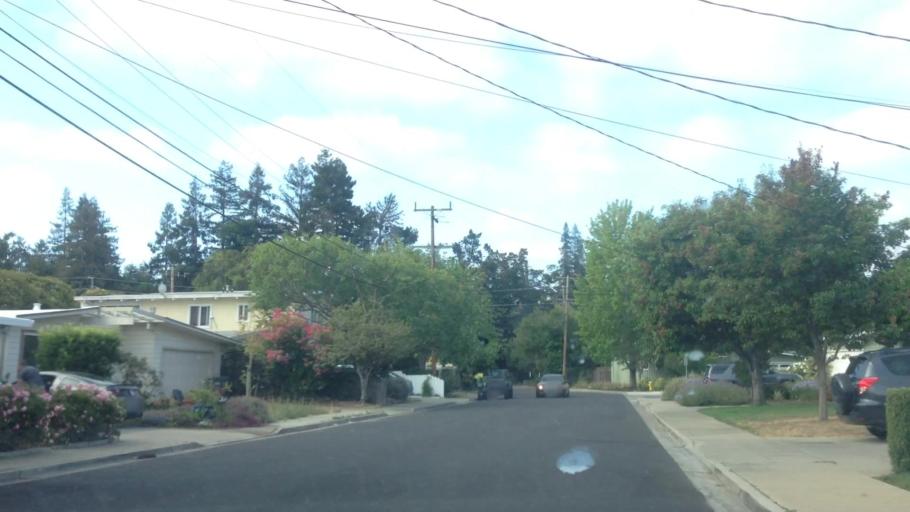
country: US
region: California
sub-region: San Mateo County
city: North Fair Oaks
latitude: 37.4777
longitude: -122.1817
